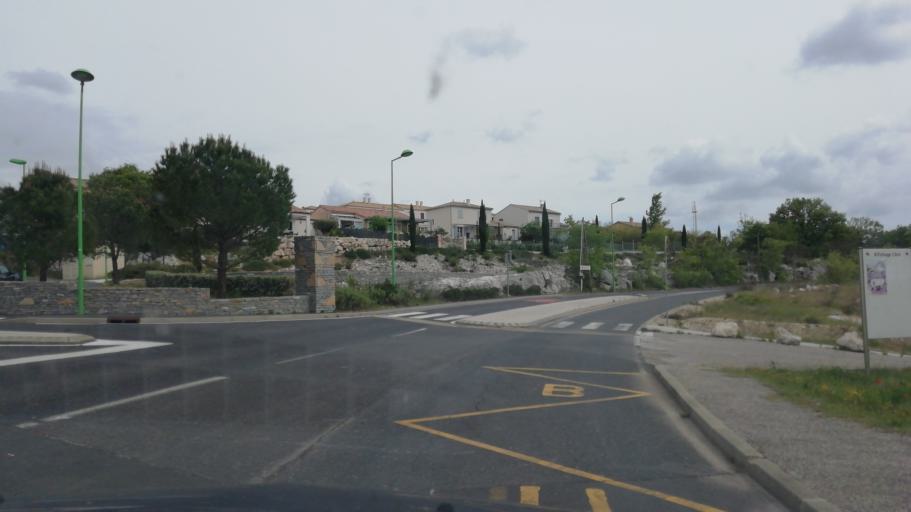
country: FR
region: Languedoc-Roussillon
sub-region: Departement de l'Herault
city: Saint-Martin-de-Londres
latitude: 43.7970
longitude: 3.7340
